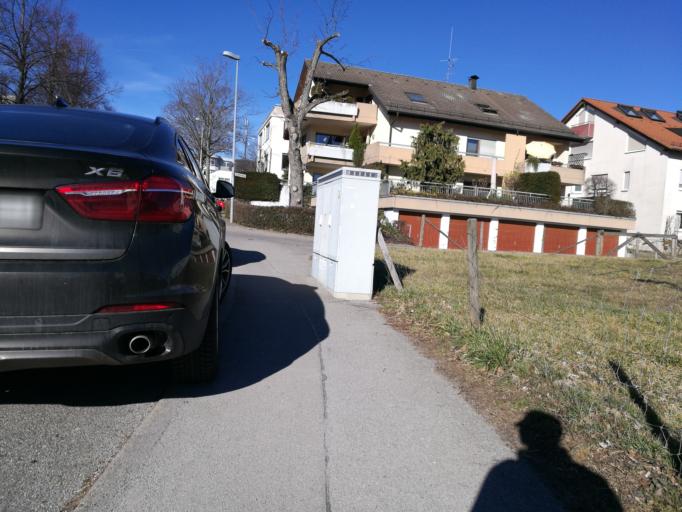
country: DE
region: Baden-Wuerttemberg
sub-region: Regierungsbezirk Stuttgart
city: Leinfelden-Echterdingen
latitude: 48.6902
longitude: 9.1609
